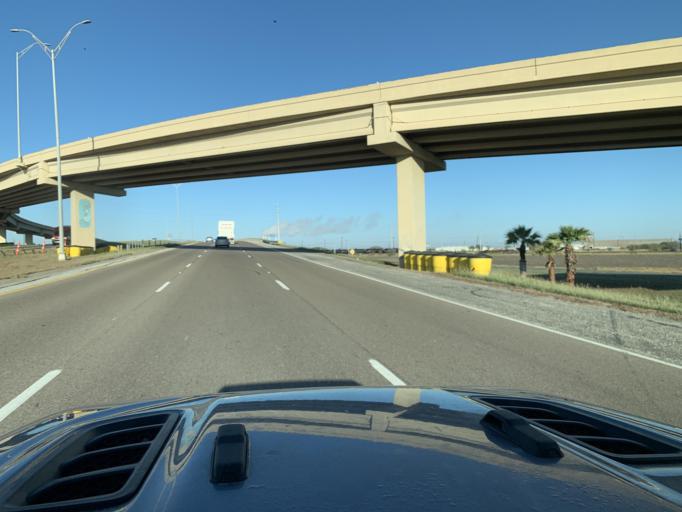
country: US
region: Texas
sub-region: Nueces County
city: Corpus Christi
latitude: 27.7831
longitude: -97.4831
